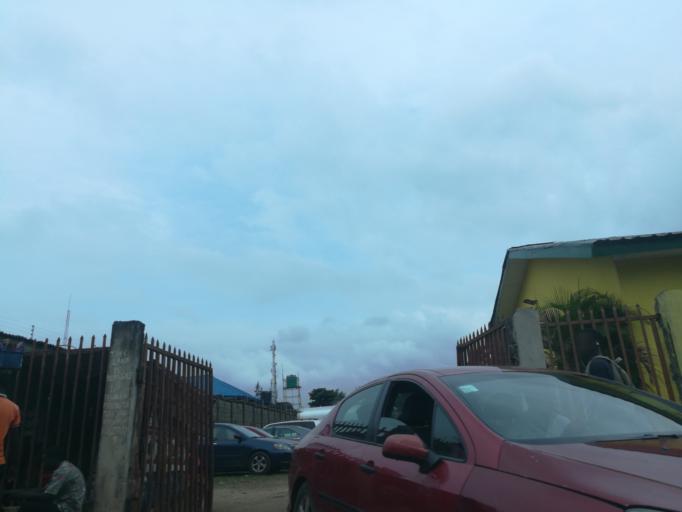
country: NG
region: Lagos
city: Ojota
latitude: 6.5741
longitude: 3.3594
